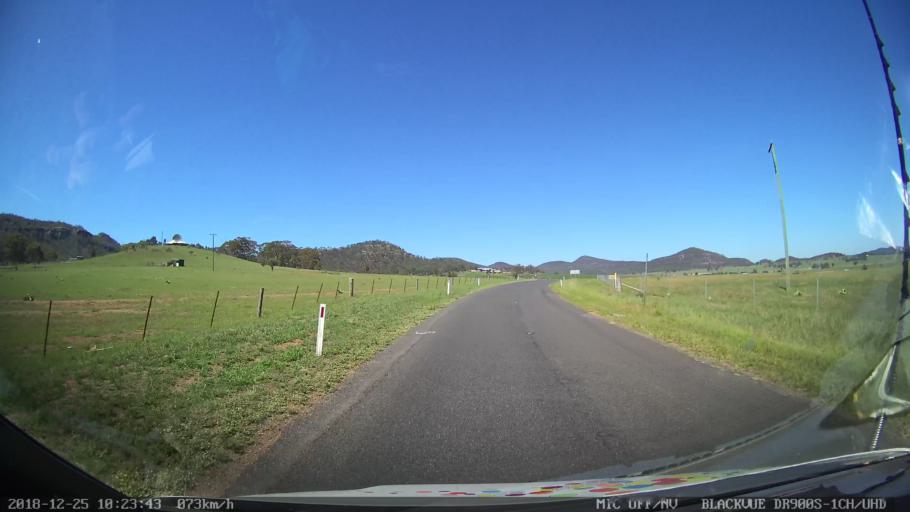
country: AU
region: New South Wales
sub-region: Muswellbrook
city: Denman
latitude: -32.3885
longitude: 150.5218
